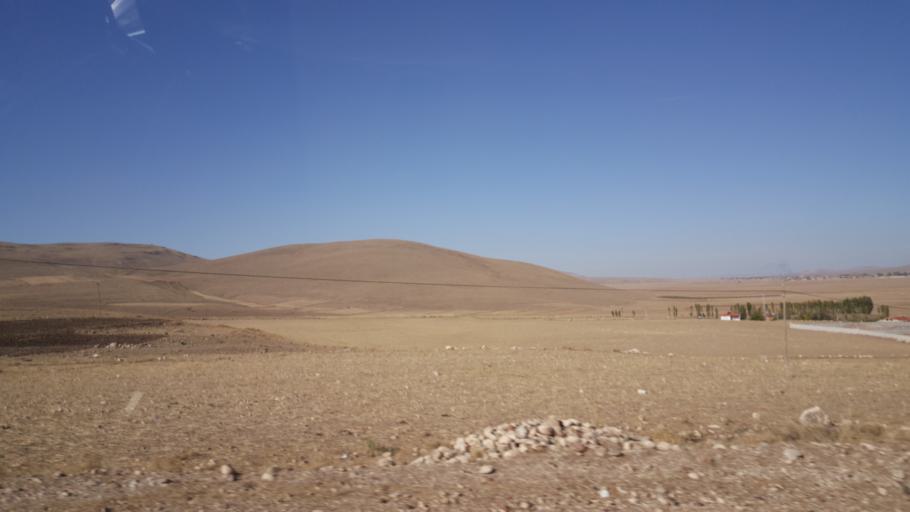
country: TR
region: Ankara
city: Altpinar
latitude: 39.1704
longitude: 32.7234
